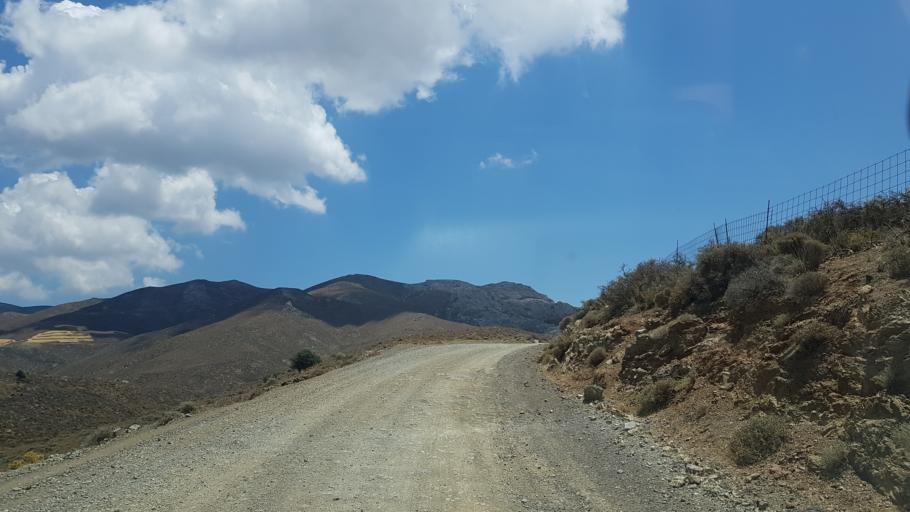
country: GR
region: Crete
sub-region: Nomos Irakleiou
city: Agioi Deka
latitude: 34.9707
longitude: 24.9822
